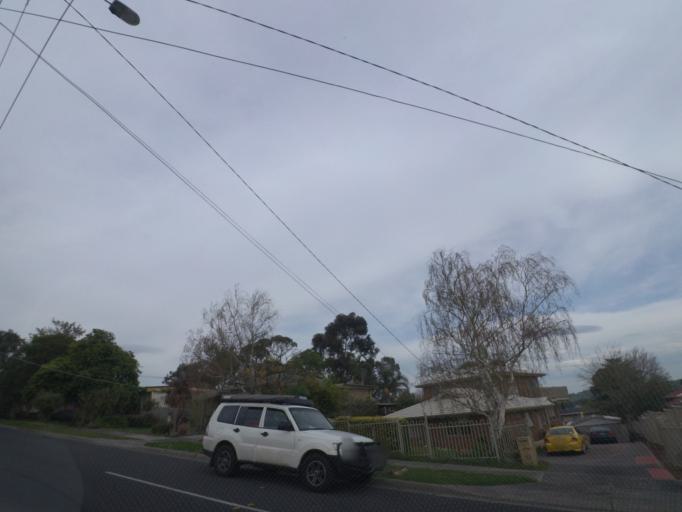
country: AU
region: Victoria
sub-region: Knox
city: Ferntree Gully
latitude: -37.8984
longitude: 145.2891
